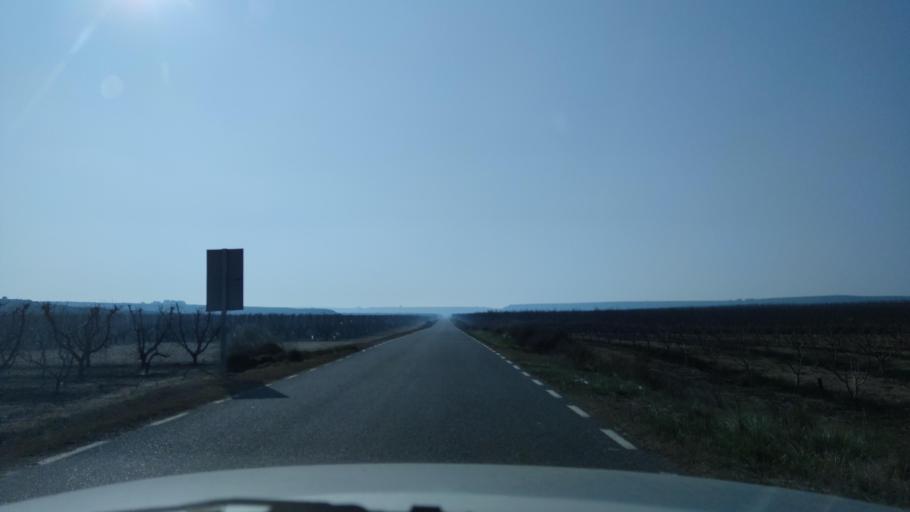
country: ES
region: Catalonia
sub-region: Provincia de Lleida
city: Sunyer
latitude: 41.5353
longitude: 0.5771
